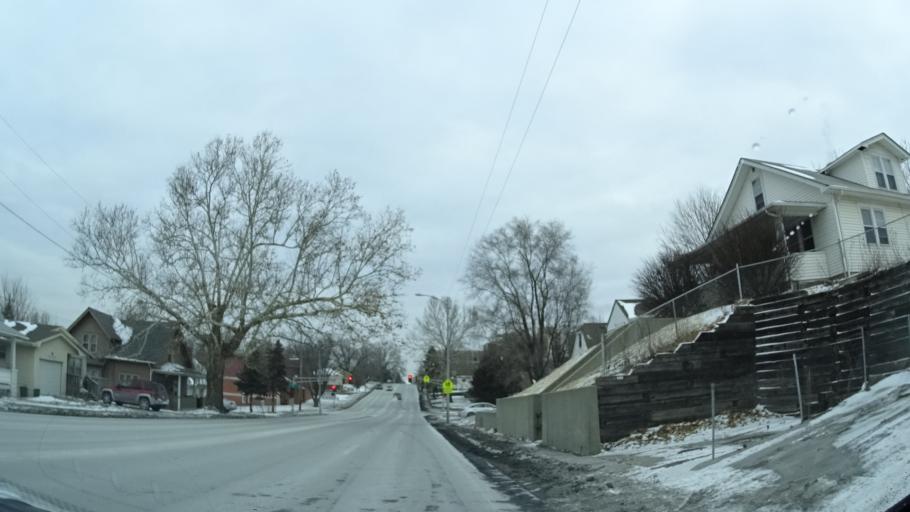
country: US
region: Nebraska
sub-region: Douglas County
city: Omaha
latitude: 41.2375
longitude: -95.9758
